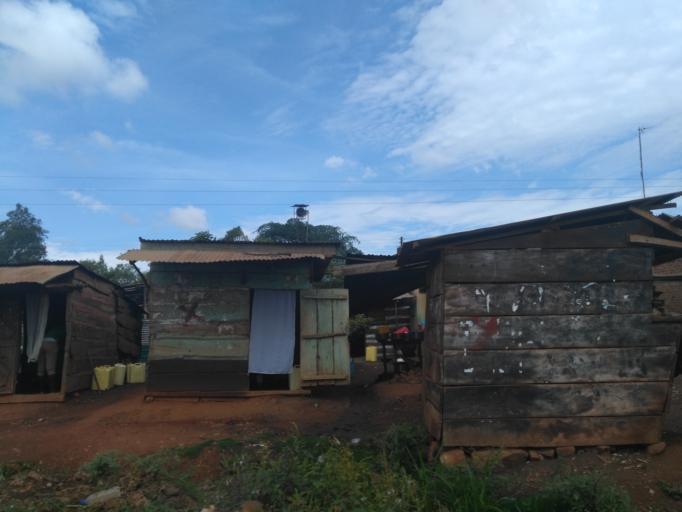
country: UG
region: Central Region
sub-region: Buikwe District
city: Njeru
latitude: 0.3959
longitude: 33.1737
